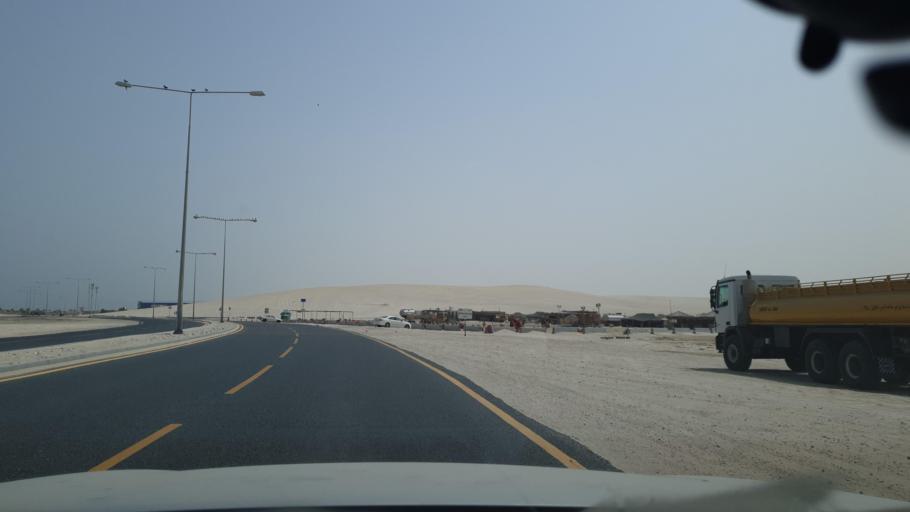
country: QA
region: Al Wakrah
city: Umm Sa'id
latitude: 24.8606
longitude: 51.5112
